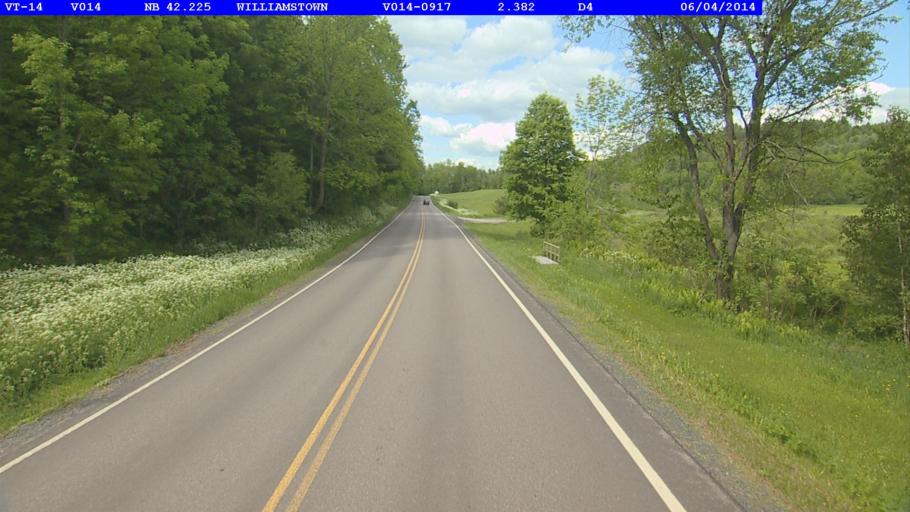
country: US
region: Vermont
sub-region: Orange County
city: Williamstown
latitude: 44.0937
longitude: -72.5498
